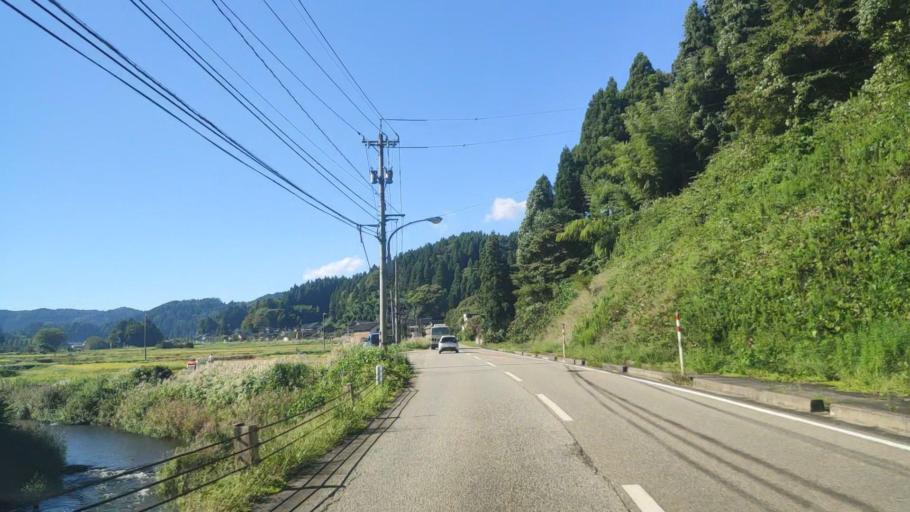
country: JP
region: Ishikawa
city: Nanao
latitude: 37.2758
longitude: 137.0536
